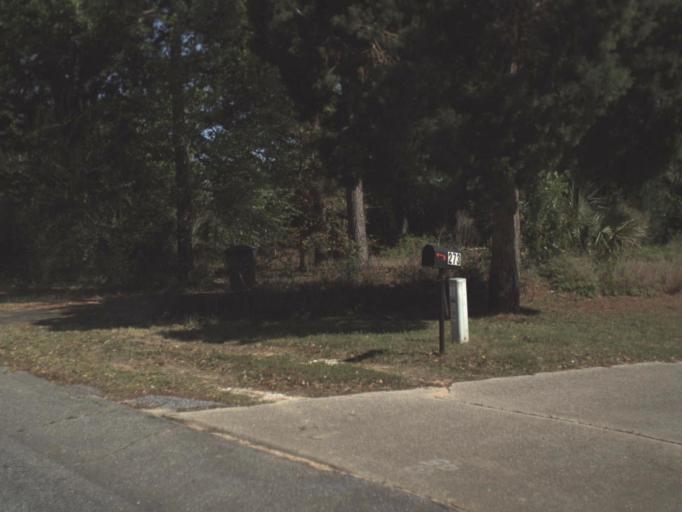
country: US
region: Florida
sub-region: Escambia County
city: Brent
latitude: 30.4964
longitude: -87.2427
